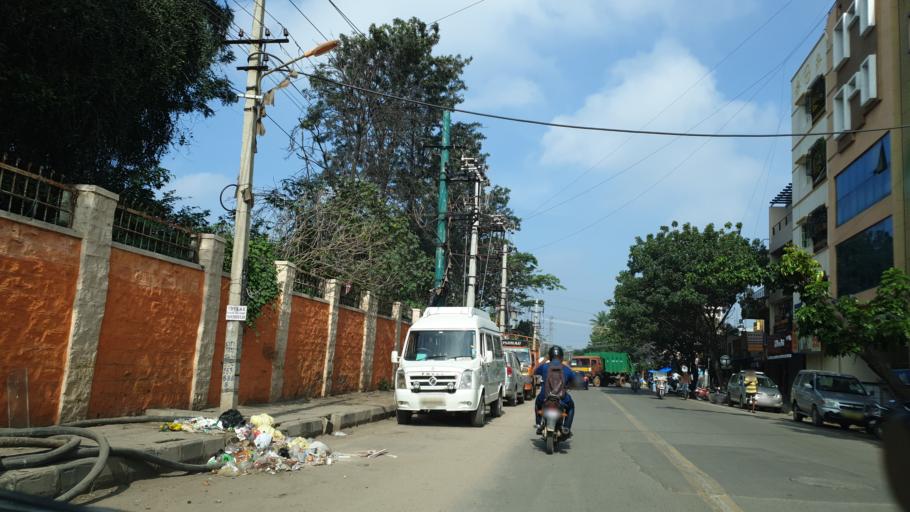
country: IN
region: Karnataka
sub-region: Bangalore Urban
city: Bangalore
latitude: 12.9742
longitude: 77.6723
